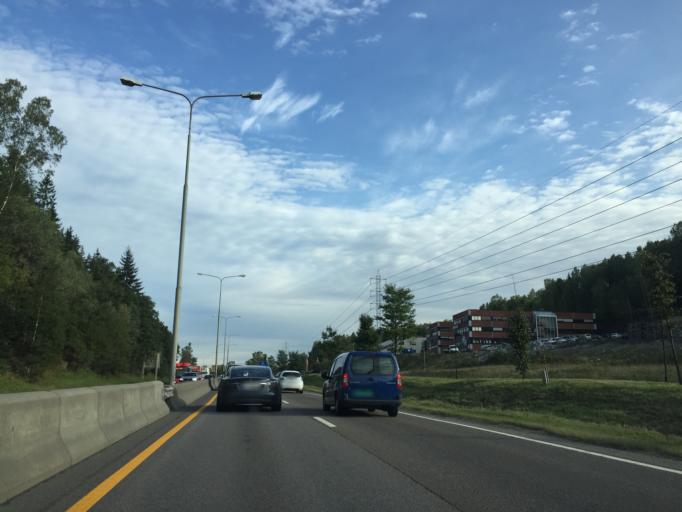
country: NO
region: Akershus
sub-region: Oppegard
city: Kolbotn
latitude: 59.8671
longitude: 10.8301
